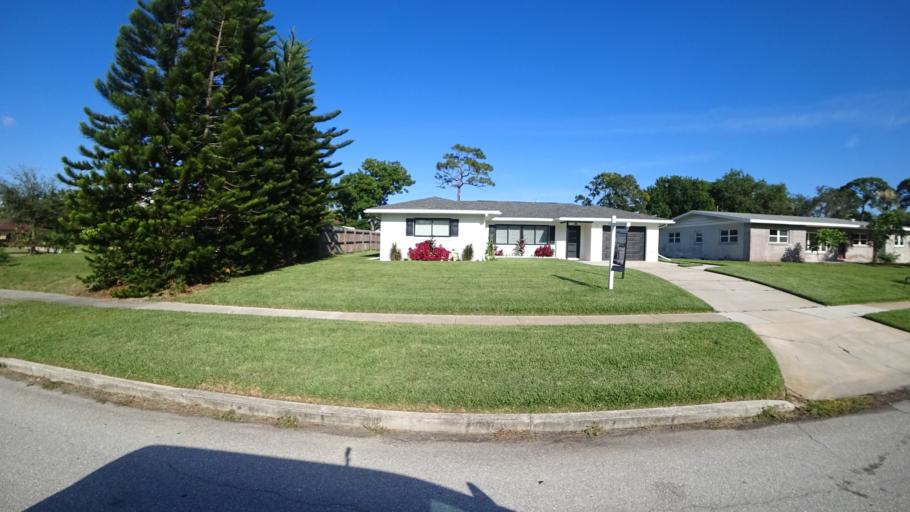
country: US
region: Florida
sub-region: Manatee County
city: West Bradenton
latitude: 27.4888
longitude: -82.6399
